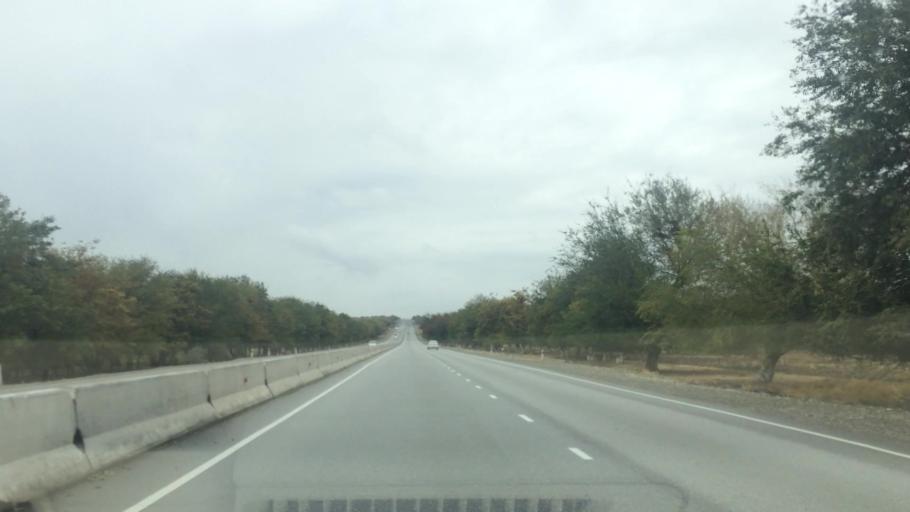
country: UZ
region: Samarqand
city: Bulung'ur
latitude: 39.8726
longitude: 67.4794
